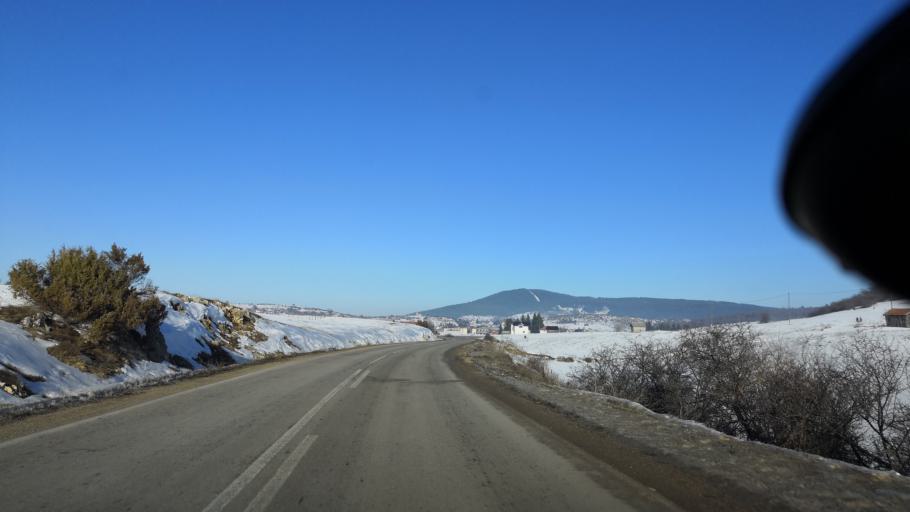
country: BA
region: Republika Srpska
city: Sokolac
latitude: 43.9370
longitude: 18.8233
